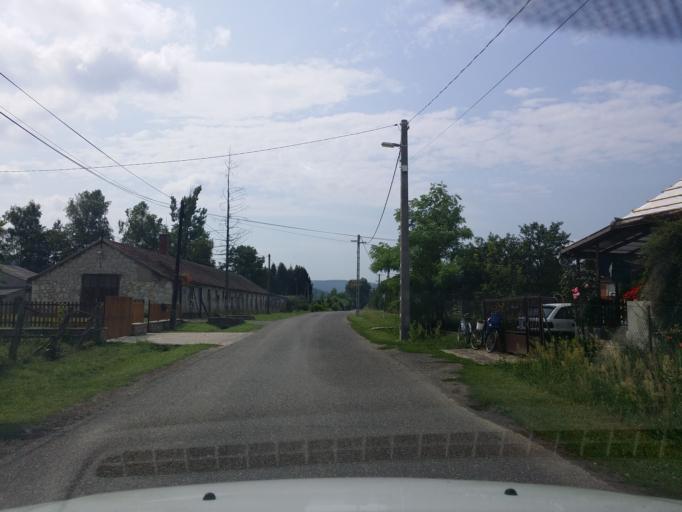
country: HU
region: Borsod-Abauj-Zemplen
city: Sarospatak
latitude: 48.4491
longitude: 21.5292
